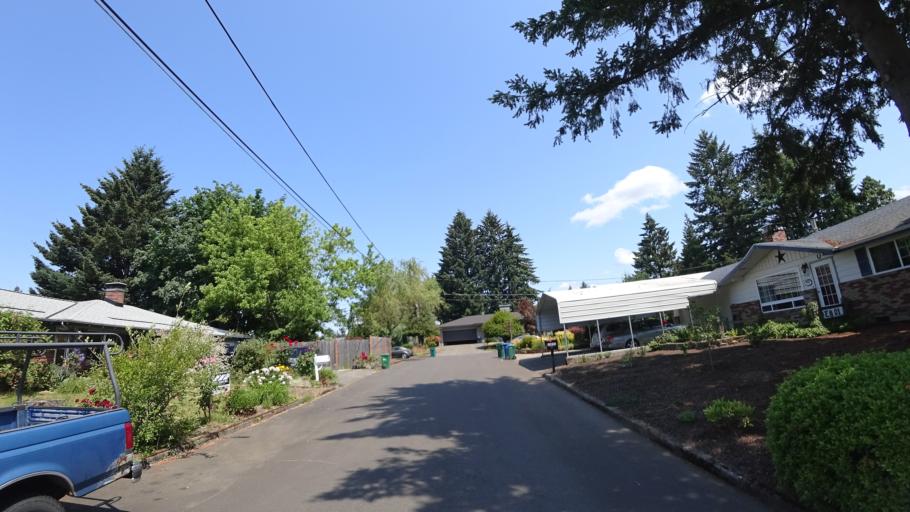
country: US
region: Oregon
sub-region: Clackamas County
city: Oatfield
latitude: 45.4443
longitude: -122.5881
